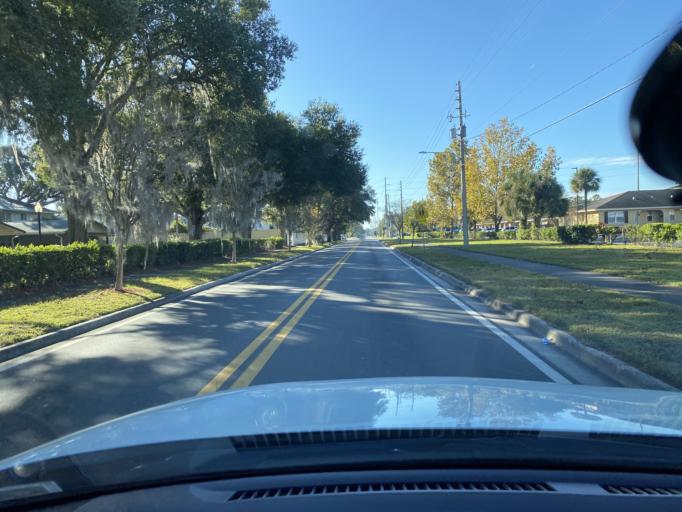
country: US
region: Florida
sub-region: Orange County
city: Azalea Park
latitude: 28.5224
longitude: -81.3022
